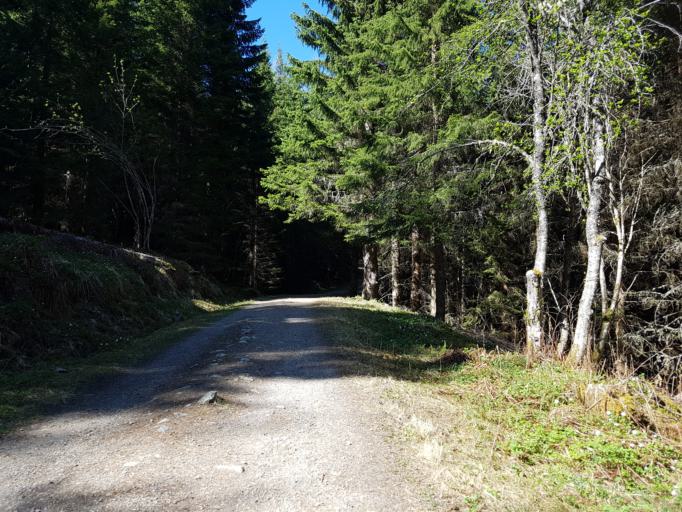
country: NO
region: Sor-Trondelag
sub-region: Trondheim
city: Trondheim
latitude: 63.4376
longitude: 10.3421
